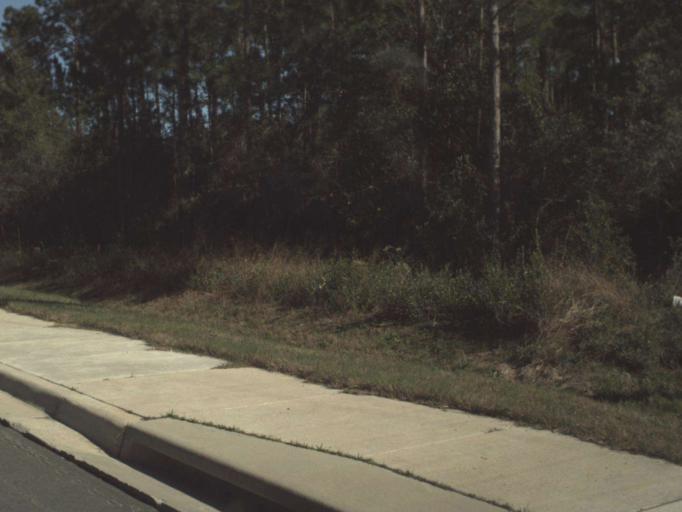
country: US
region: Florida
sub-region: Santa Rosa County
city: Bagdad
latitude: 30.5398
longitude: -87.0872
